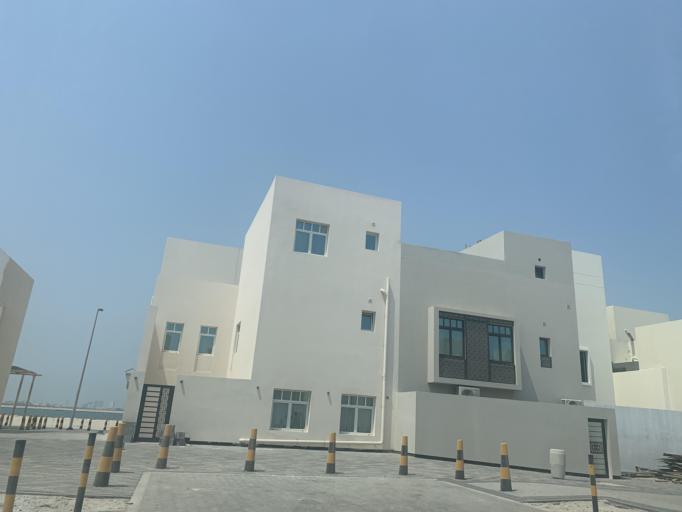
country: BH
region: Muharraq
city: Al Hadd
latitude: 26.2442
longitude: 50.6650
